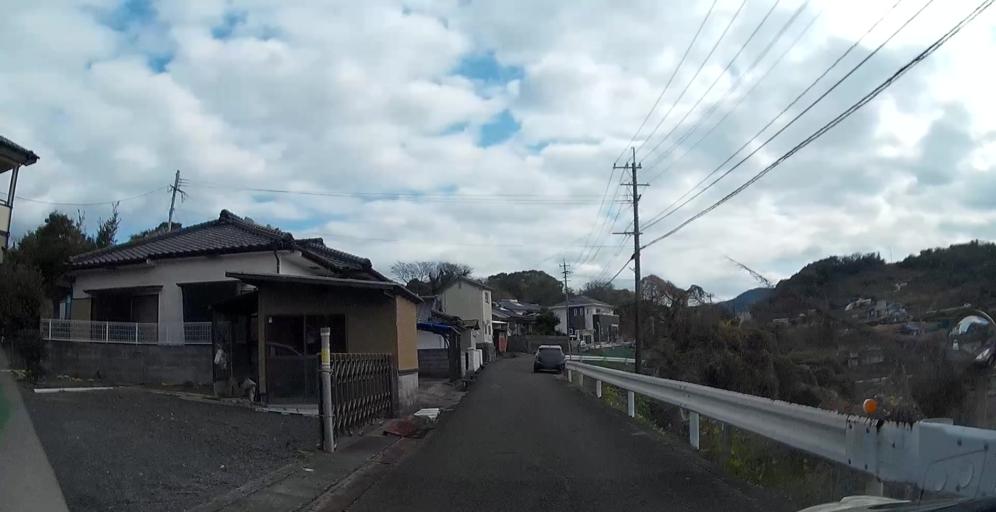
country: JP
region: Kumamoto
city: Minamata
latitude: 32.2089
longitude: 130.3853
